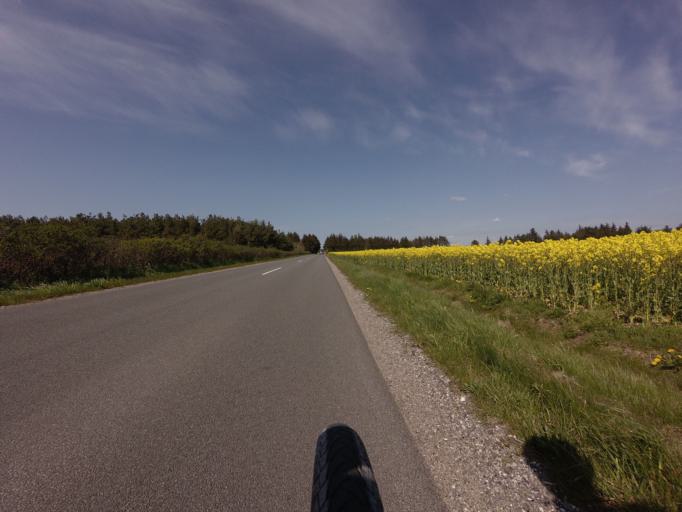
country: DK
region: North Denmark
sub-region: Jammerbugt Kommune
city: Pandrup
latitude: 57.2263
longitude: 9.6046
